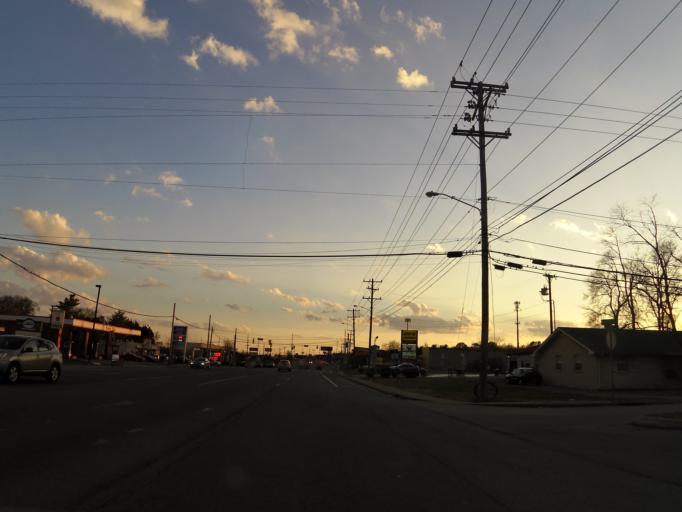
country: US
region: Tennessee
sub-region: Davidson County
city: Lakewood
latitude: 36.2022
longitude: -86.6170
